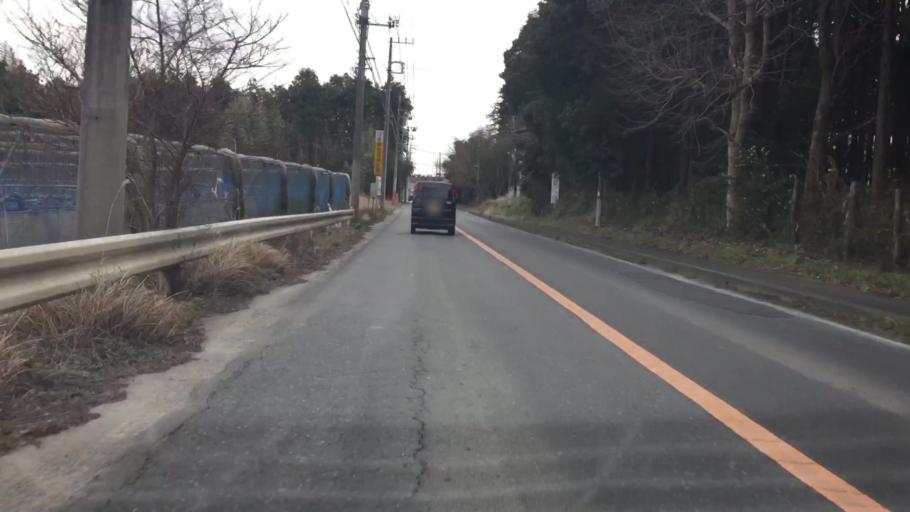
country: JP
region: Ibaraki
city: Ryugasaki
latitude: 35.8259
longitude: 140.1636
